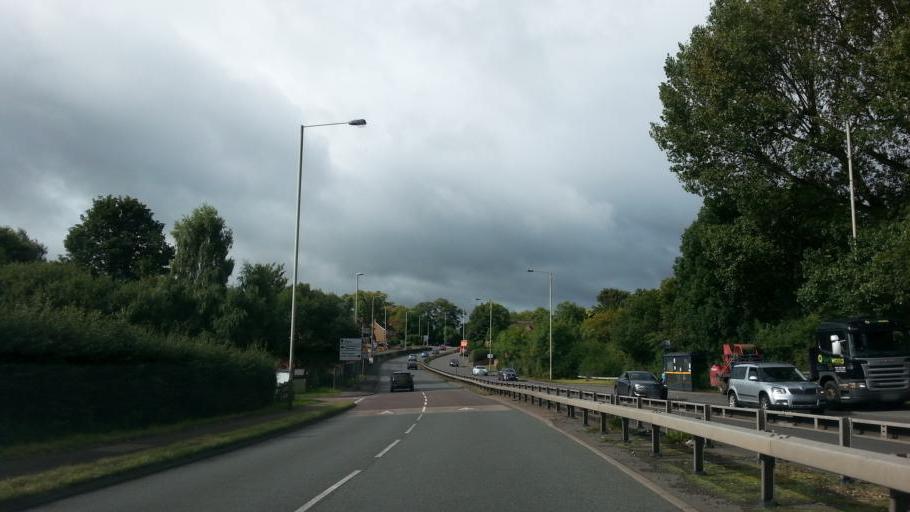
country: GB
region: England
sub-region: Dudley
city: Halesowen
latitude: 52.4456
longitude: -2.0406
